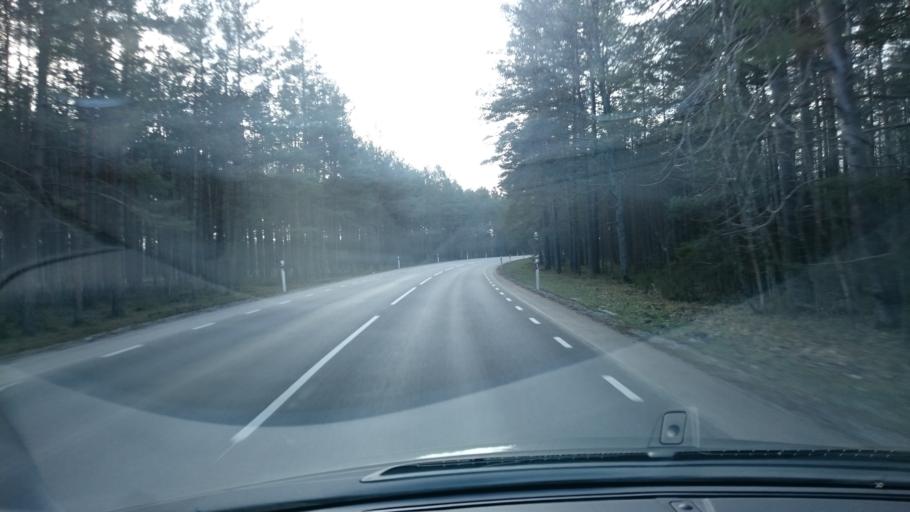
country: EE
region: Harju
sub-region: Paldiski linn
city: Paldiski
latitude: 59.3899
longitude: 24.2412
